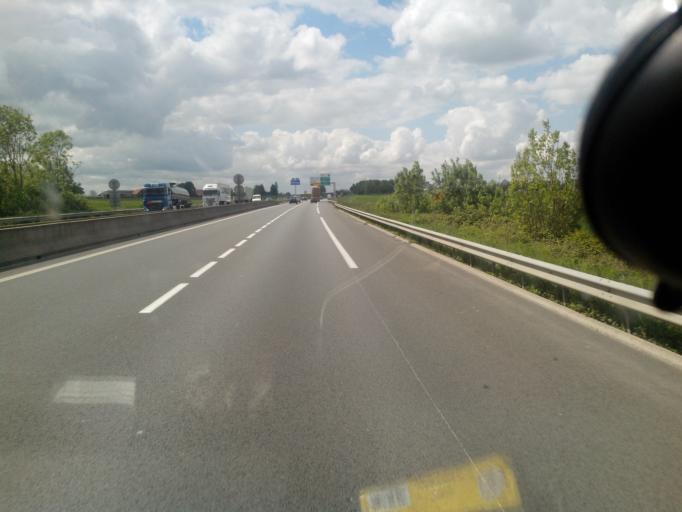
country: FR
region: Nord-Pas-de-Calais
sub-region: Departement du Nord
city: Meteren
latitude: 50.7305
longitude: 2.7058
